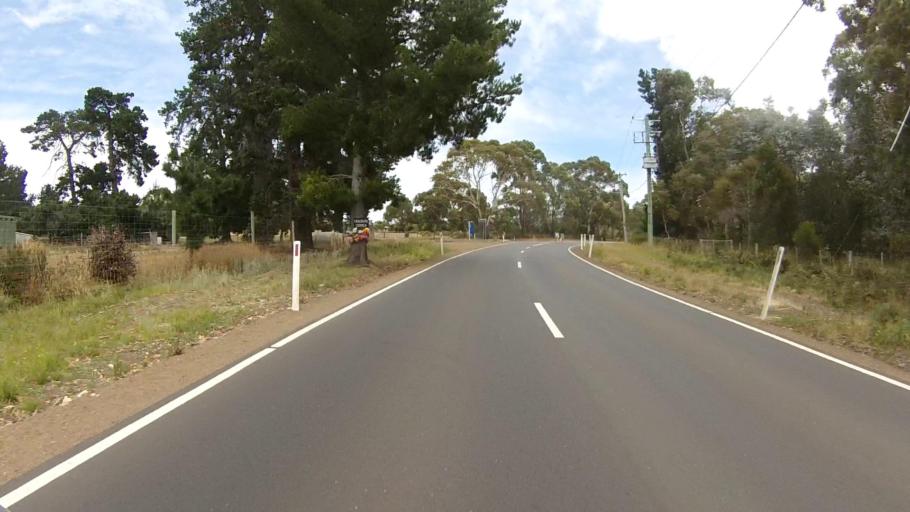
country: AU
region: Tasmania
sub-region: Clarence
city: Acton Park
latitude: -42.8672
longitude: 147.4875
